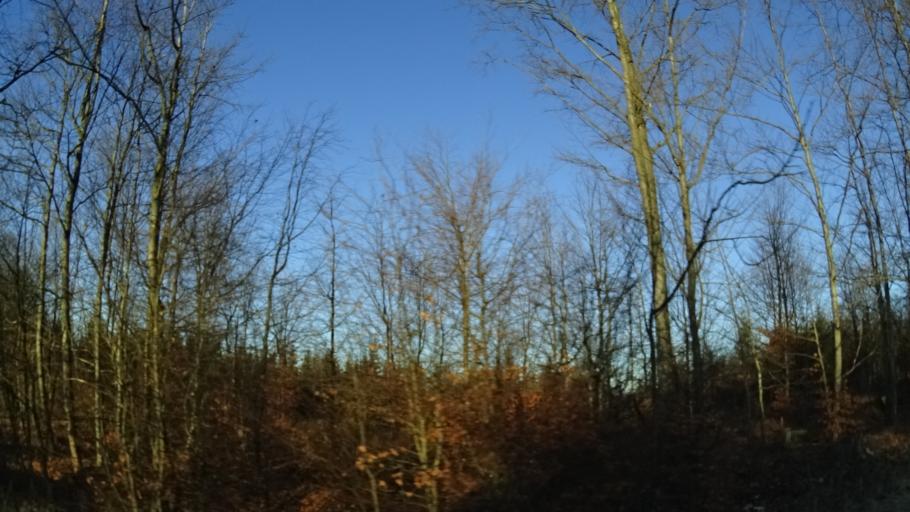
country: DE
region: Thuringia
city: Judenbach
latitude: 50.4258
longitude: 11.2337
